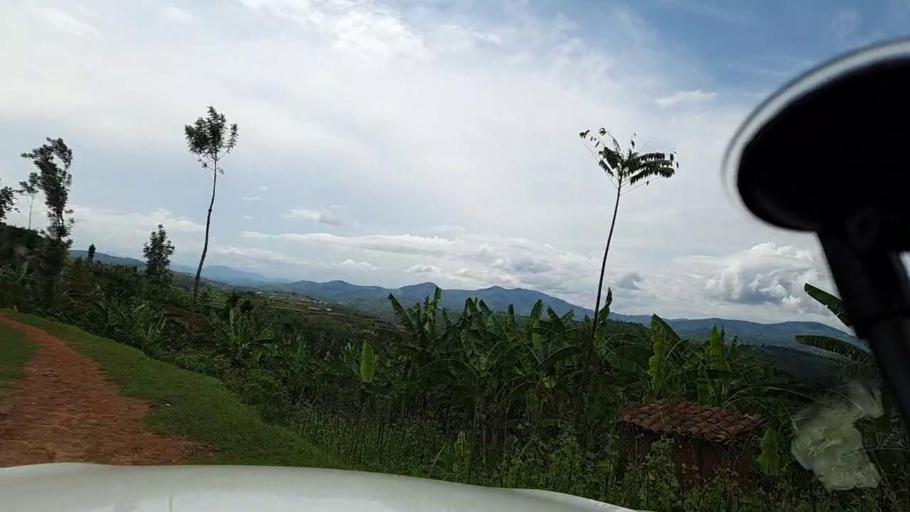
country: RW
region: Southern Province
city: Gitarama
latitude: -2.0642
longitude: 29.6454
